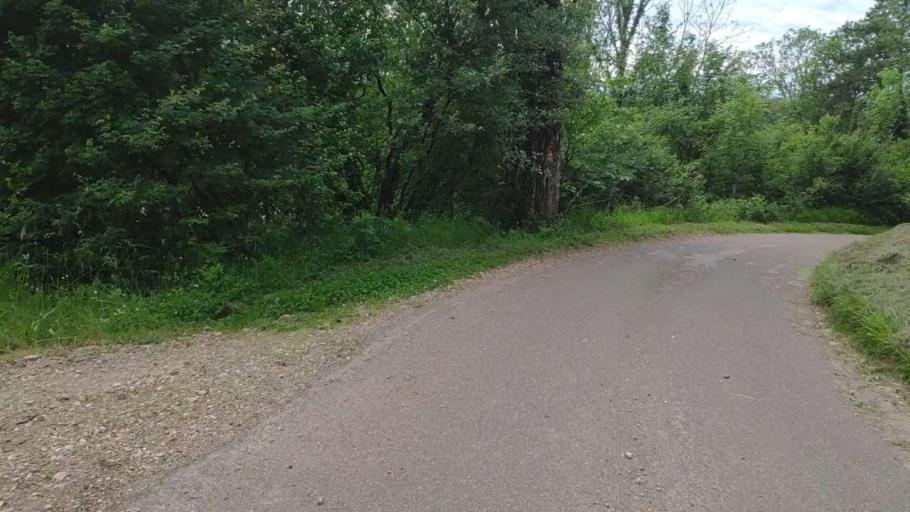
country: FR
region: Franche-Comte
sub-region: Departement du Jura
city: Montmorot
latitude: 46.7835
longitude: 5.5672
